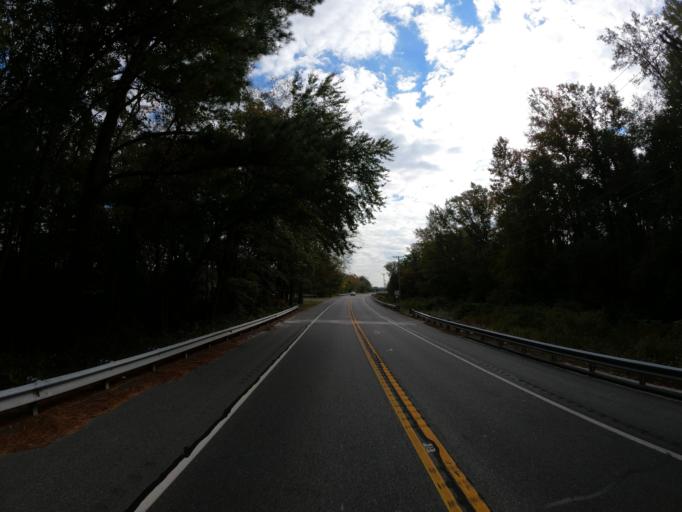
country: US
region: Delaware
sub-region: Sussex County
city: Bridgeville
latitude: 38.7089
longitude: -75.5236
